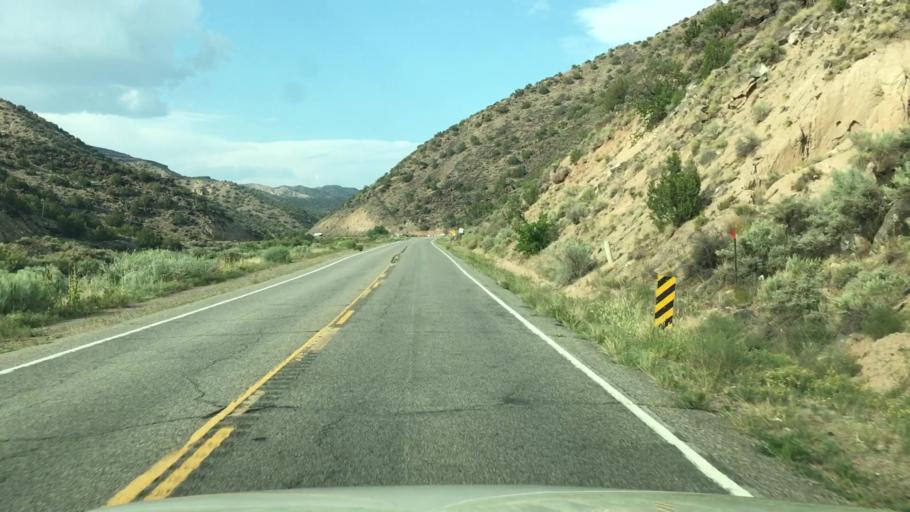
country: US
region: New Mexico
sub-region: Rio Arriba County
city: Ohkay Owingeh
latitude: 36.1944
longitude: -105.9753
